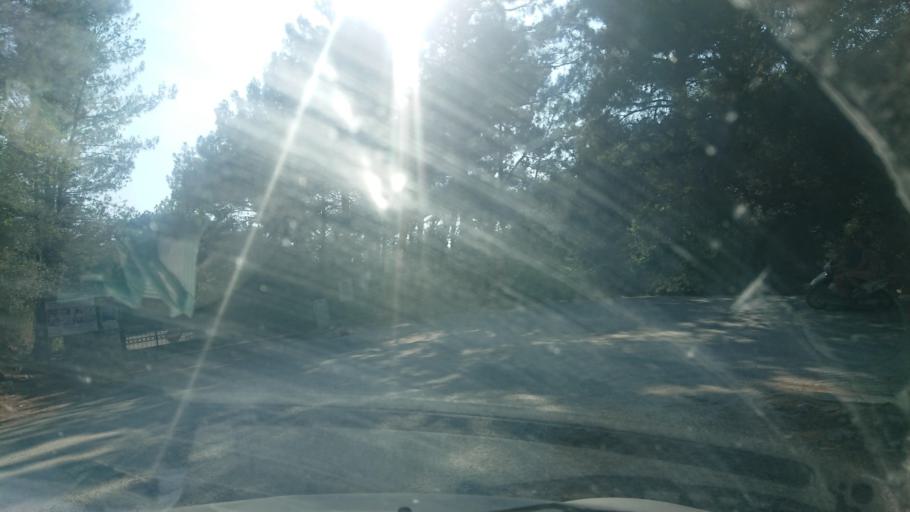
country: TR
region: Aydin
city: Atburgazi
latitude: 37.6887
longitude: 27.1247
